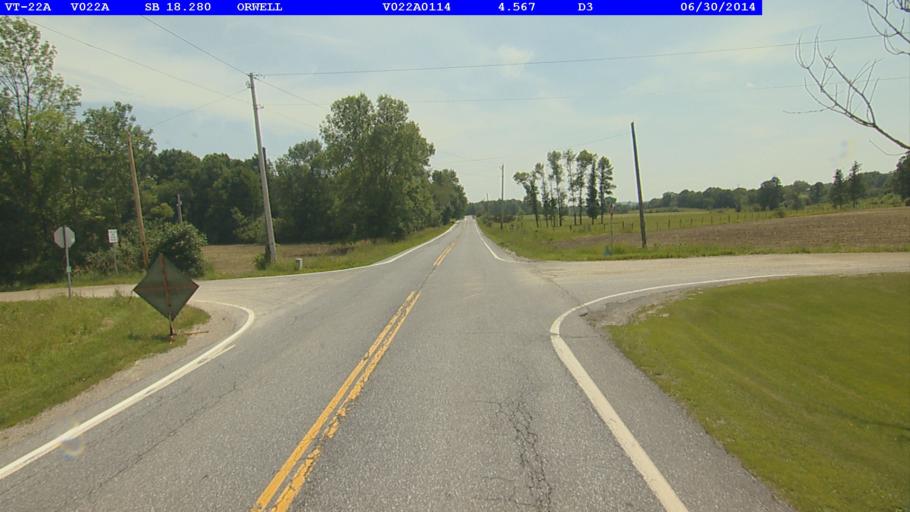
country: US
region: New York
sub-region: Essex County
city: Ticonderoga
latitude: 43.8227
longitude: -73.3069
